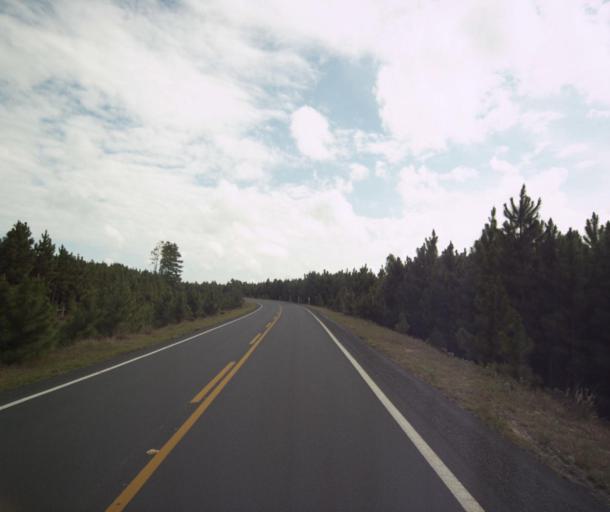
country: BR
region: Rio Grande do Sul
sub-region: Sao Lourenco Do Sul
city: Sao Lourenco do Sul
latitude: -31.4631
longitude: -51.2306
